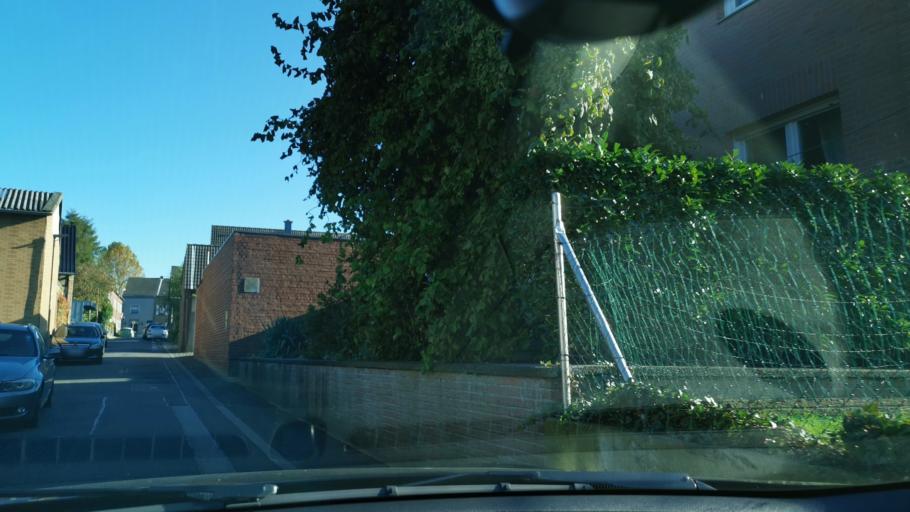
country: DE
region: North Rhine-Westphalia
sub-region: Regierungsbezirk Dusseldorf
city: Rommerskirchen
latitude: 51.0476
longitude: 6.7097
